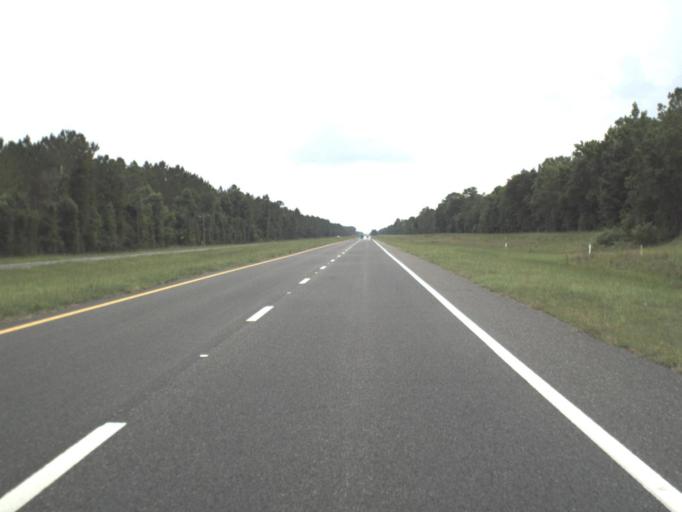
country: US
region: Florida
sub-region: Levy County
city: Chiefland
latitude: 29.3833
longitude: -82.8026
